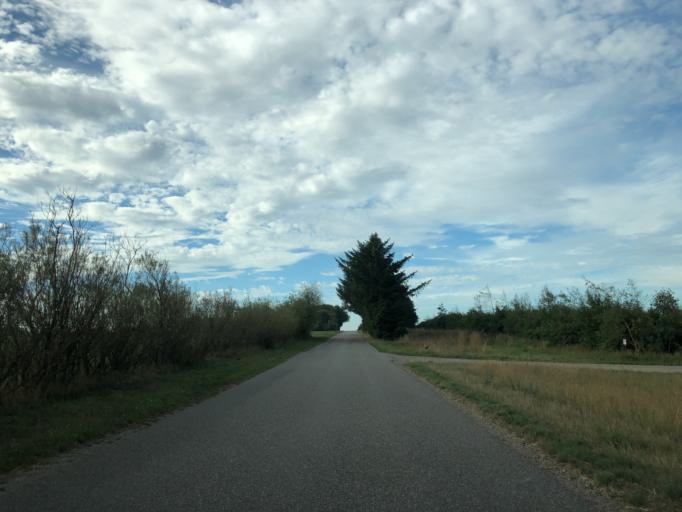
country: DK
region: Central Jutland
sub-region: Holstebro Kommune
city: Ulfborg
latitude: 56.1530
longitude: 8.4070
